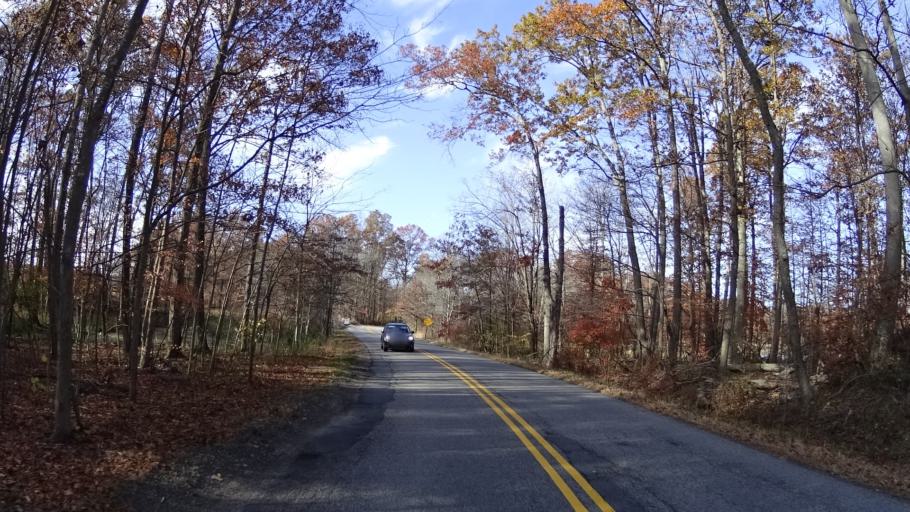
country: US
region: New Jersey
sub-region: Union County
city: Berkeley Heights
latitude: 40.7180
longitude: -74.4884
